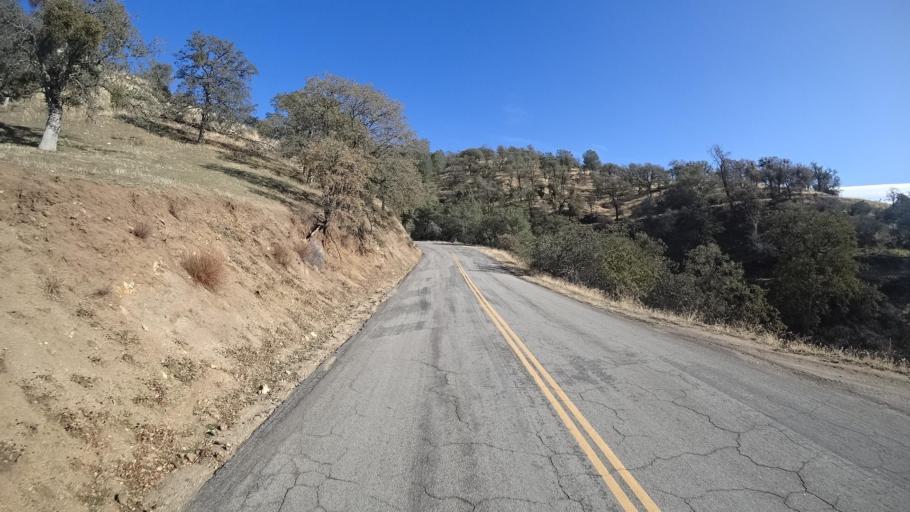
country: US
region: California
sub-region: Kern County
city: Bear Valley Springs
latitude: 35.3387
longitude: -118.5781
